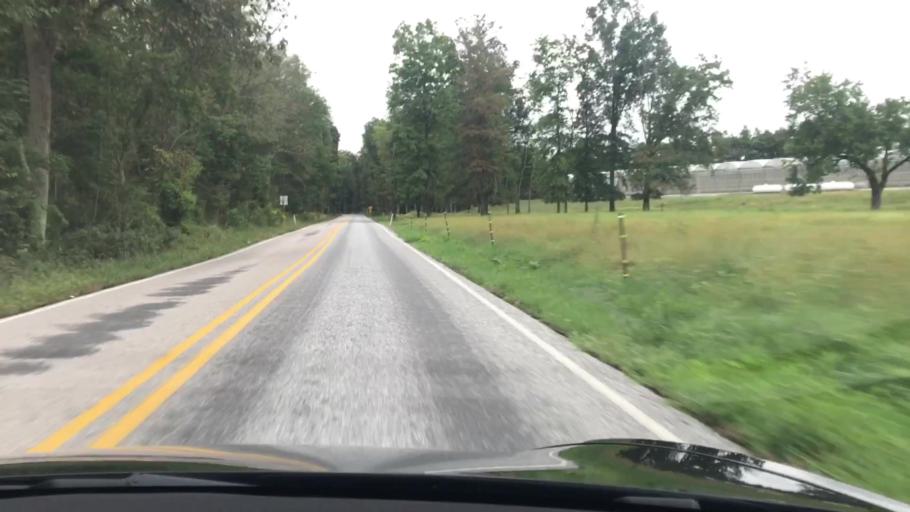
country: US
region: Pennsylvania
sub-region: York County
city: Dillsburg
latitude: 40.0610
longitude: -77.0767
